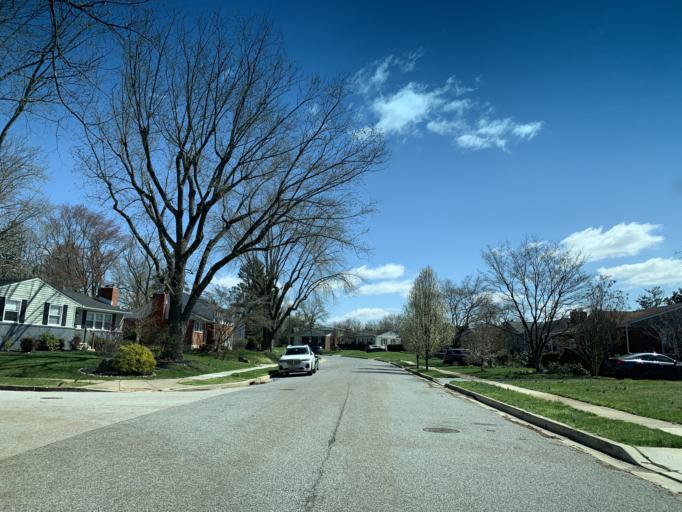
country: US
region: Maryland
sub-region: Baltimore County
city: Timonium
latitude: 39.4418
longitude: -76.6088
